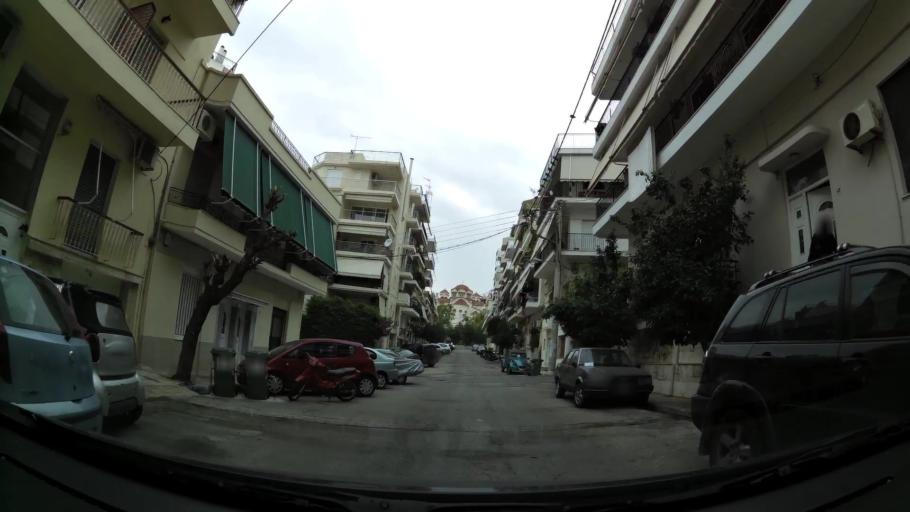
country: GR
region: Attica
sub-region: Nomos Attikis
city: Piraeus
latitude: 37.9294
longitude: 23.6314
